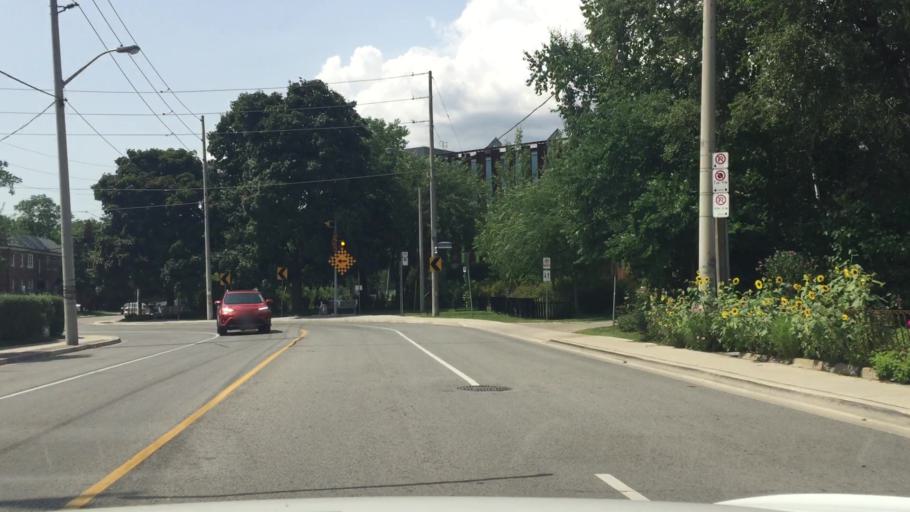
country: CA
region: Ontario
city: Toronto
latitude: 43.6923
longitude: -79.3552
